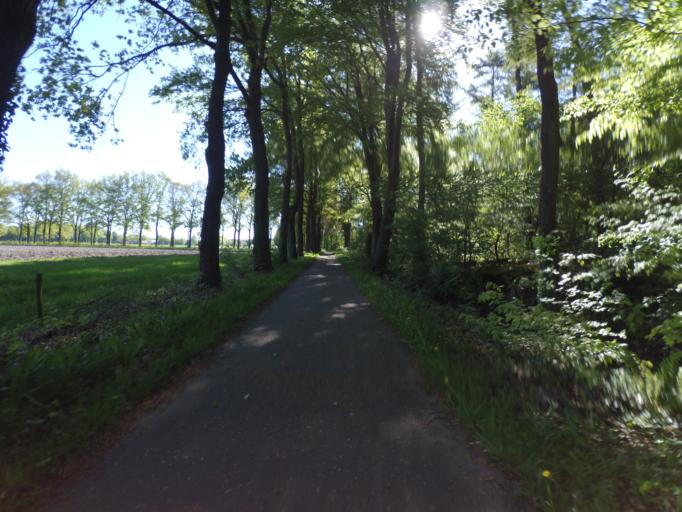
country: NL
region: Gelderland
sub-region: Gemeente Brummen
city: Brummen
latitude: 52.0921
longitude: 6.1366
